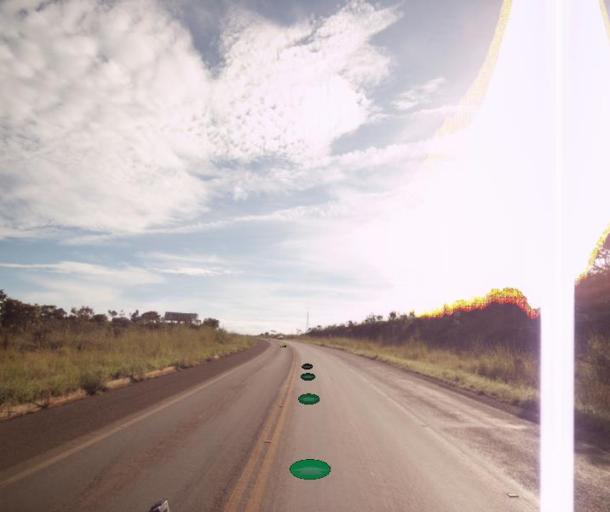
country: BR
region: Federal District
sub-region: Brasilia
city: Brasilia
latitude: -15.7514
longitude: -48.4128
